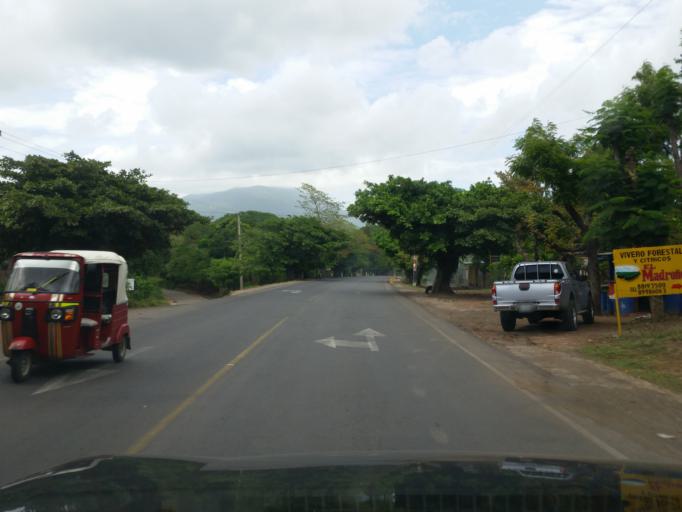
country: NI
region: Granada
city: Diriomo
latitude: 11.8751
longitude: -86.0427
